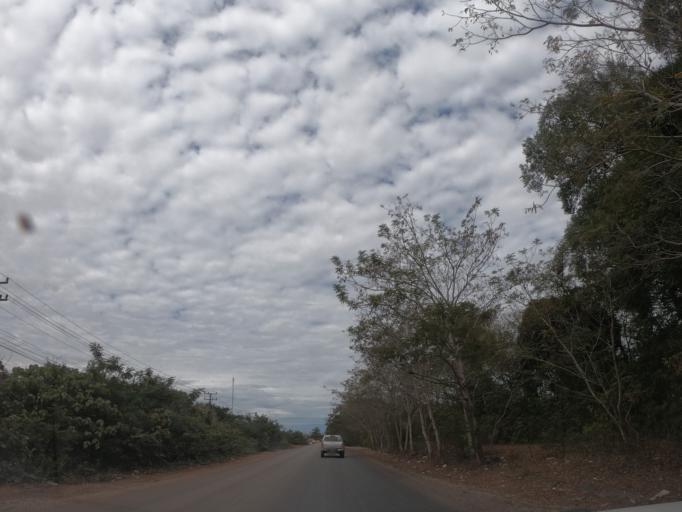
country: TH
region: Nakhon Phanom
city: Nakhon Phanom
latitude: 17.5224
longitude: 104.7267
